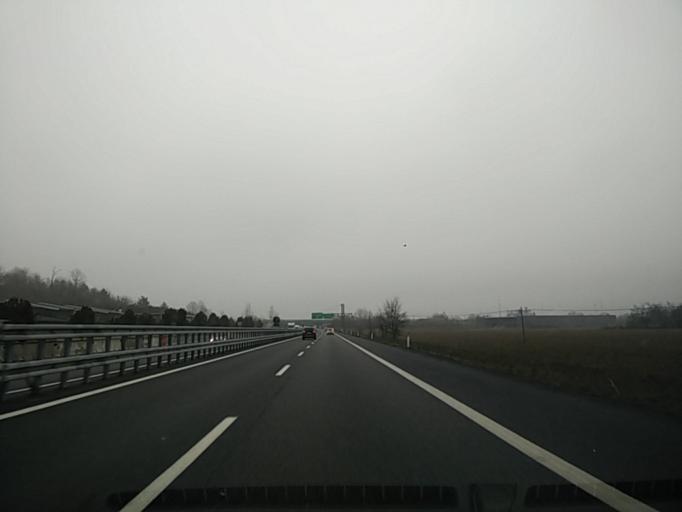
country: IT
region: Piedmont
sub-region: Provincia di Asti
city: Asti
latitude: 44.9118
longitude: 8.2366
